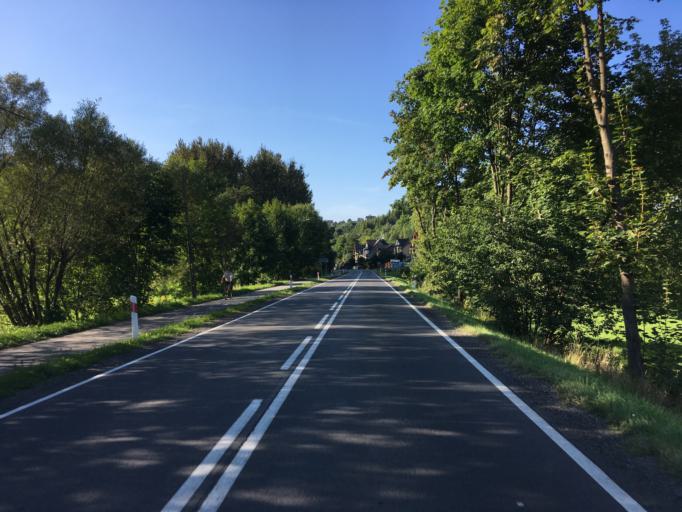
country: PL
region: Lesser Poland Voivodeship
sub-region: Powiat nowotarski
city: Kroscienko nad Dunajcem
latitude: 49.4332
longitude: 20.4406
